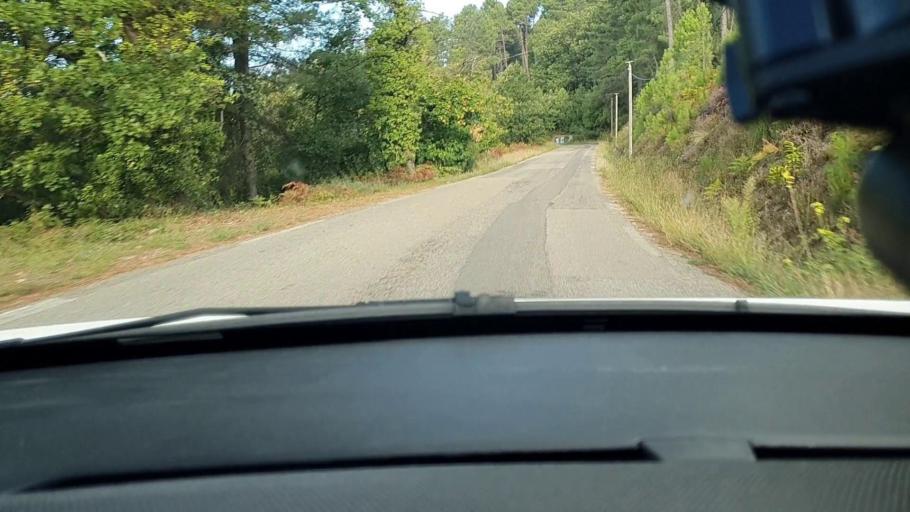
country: FR
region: Languedoc-Roussillon
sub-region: Departement du Gard
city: Besseges
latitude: 44.3254
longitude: 4.0160
